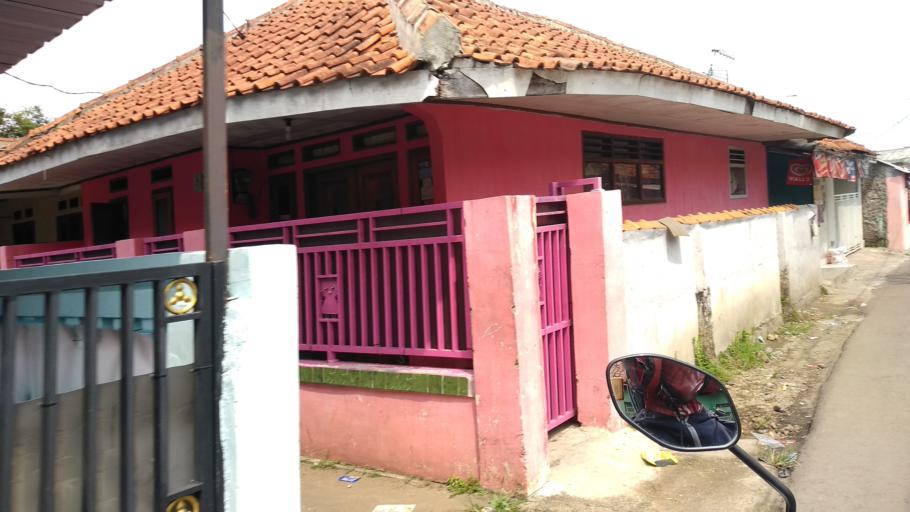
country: ID
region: West Java
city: Ciampea
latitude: -6.5626
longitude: 106.7457
